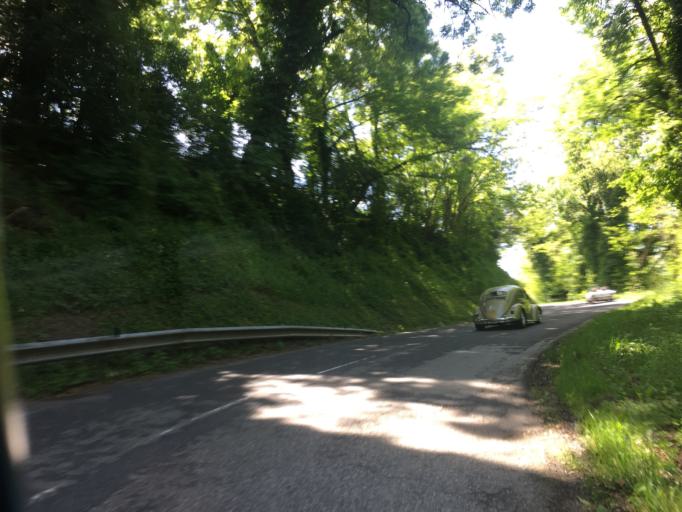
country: FR
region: Rhone-Alpes
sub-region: Departement de la Haute-Savoie
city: Marcellaz-Albanais
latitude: 45.9146
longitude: 5.9849
